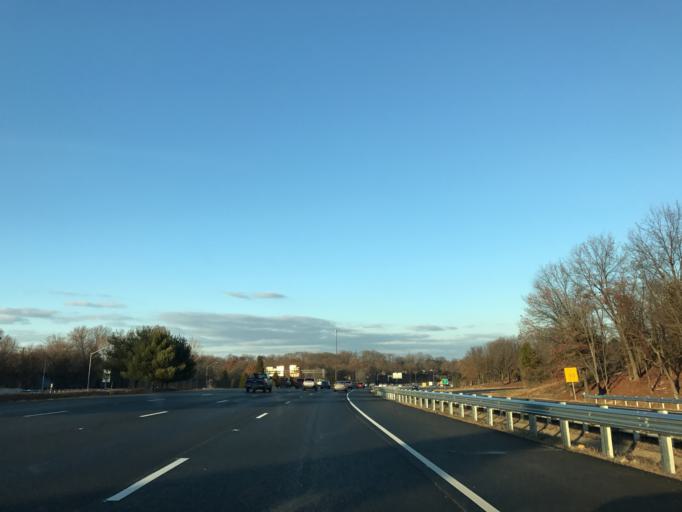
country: US
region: Maryland
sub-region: Prince George's County
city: West Laurel
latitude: 39.1006
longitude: -76.8892
